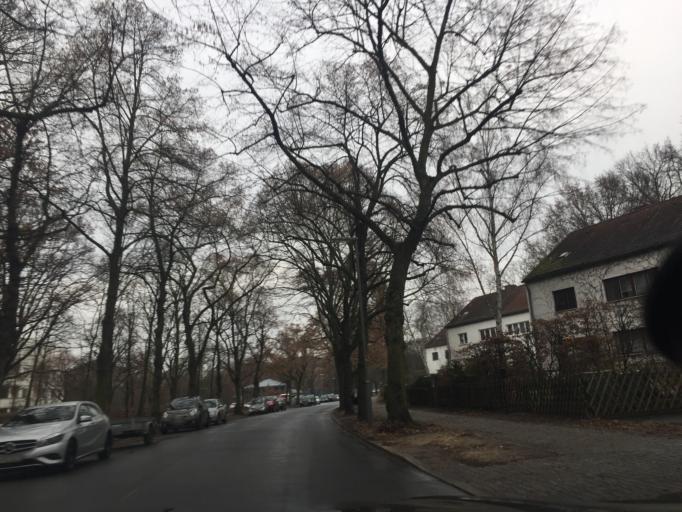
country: DE
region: Berlin
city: Haselhorst
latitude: 52.5084
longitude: 13.2284
